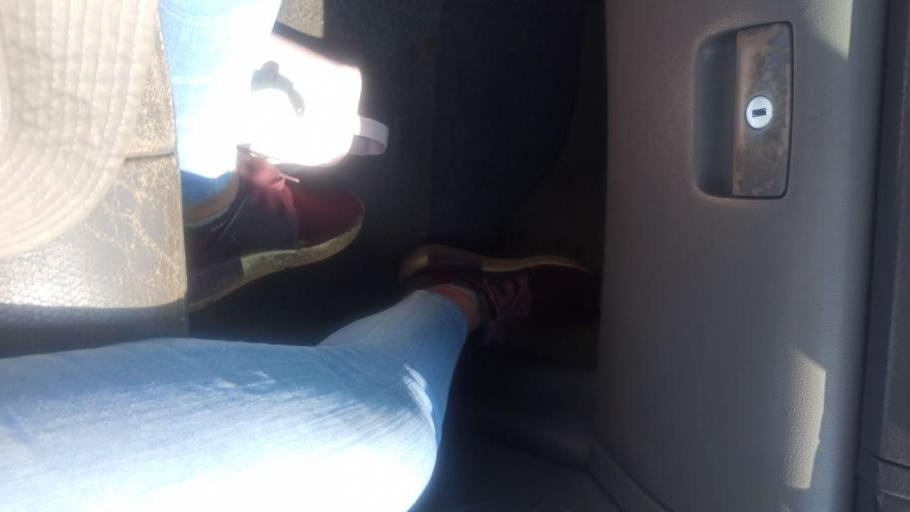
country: CO
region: Cauca
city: Buenos Aires
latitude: 3.1275
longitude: -76.5999
